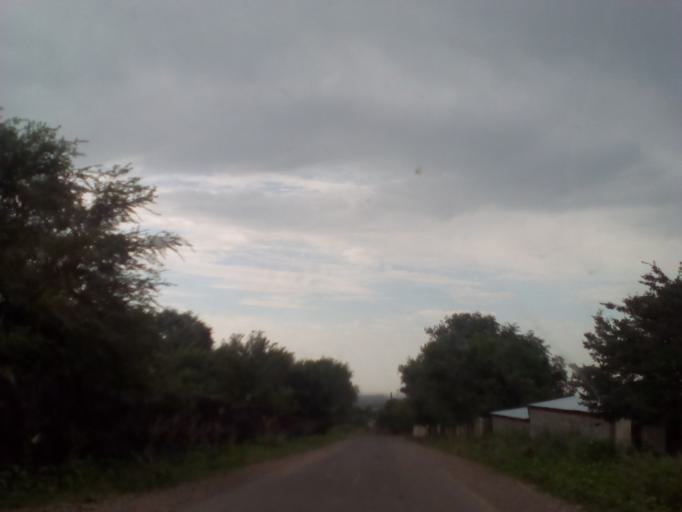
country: KZ
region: Almaty Oblysy
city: Burunday
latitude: 43.1561
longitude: 76.3846
